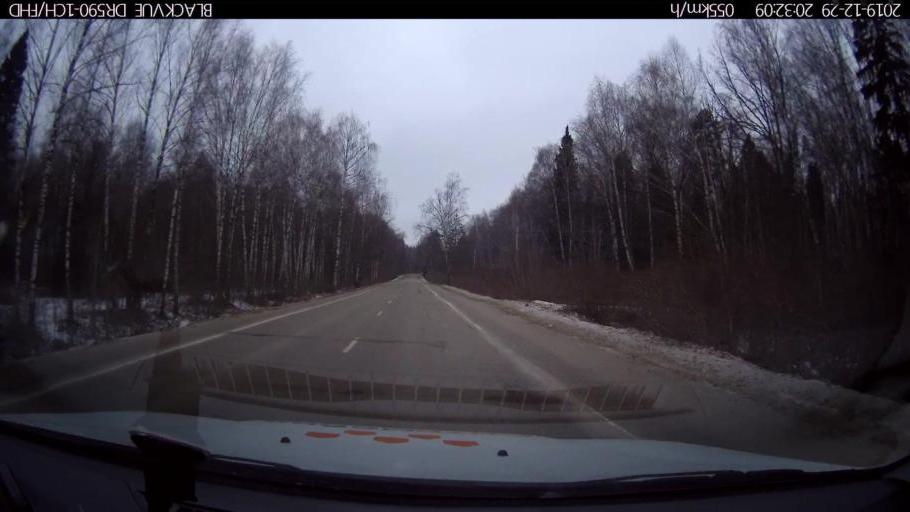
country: RU
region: Nizjnij Novgorod
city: Afonino
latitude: 56.1760
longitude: 44.0682
